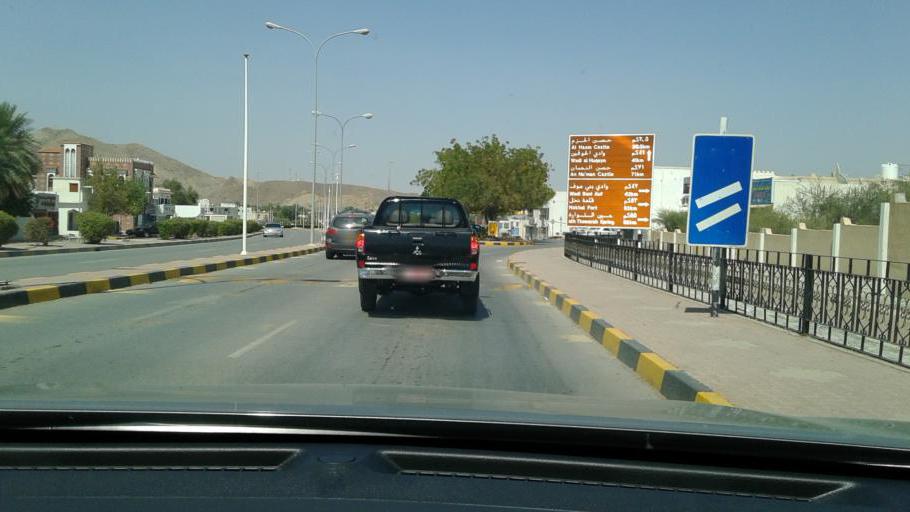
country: OM
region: Al Batinah
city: Rustaq
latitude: 23.4017
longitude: 57.4209
